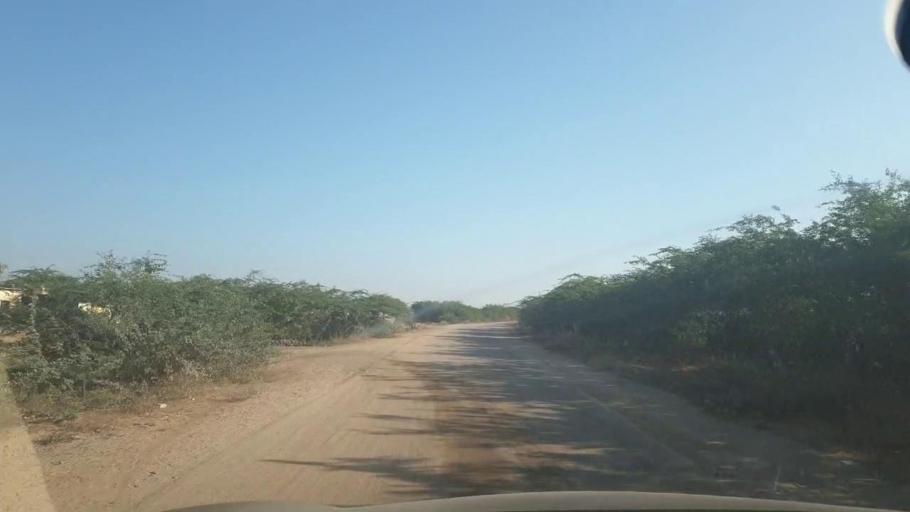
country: PK
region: Sindh
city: Malir Cantonment
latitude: 25.1115
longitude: 67.2673
